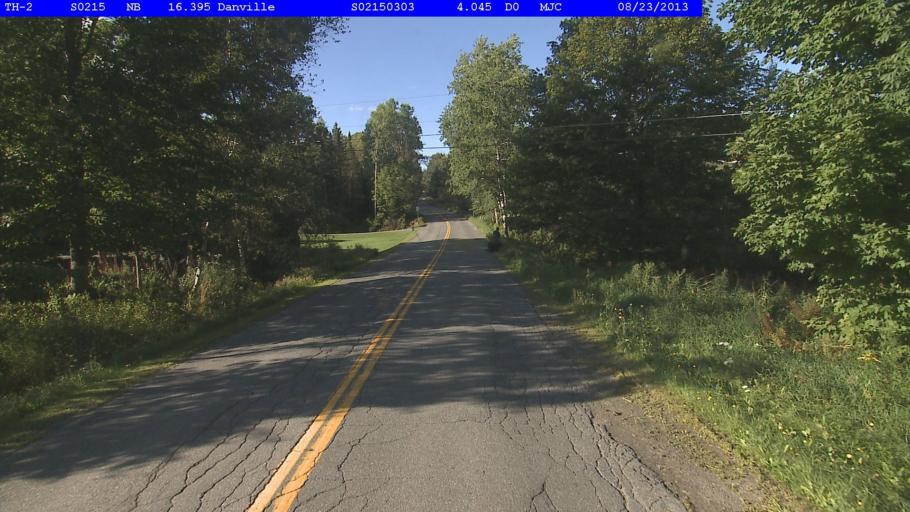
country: US
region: Vermont
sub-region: Caledonia County
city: St Johnsbury
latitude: 44.4223
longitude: -72.1421
